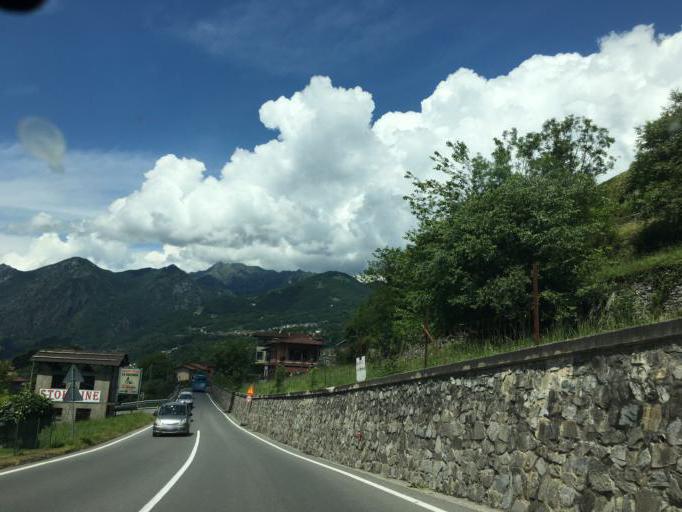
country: IT
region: Lombardy
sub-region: Provincia di Como
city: Bene Lario
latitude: 46.0392
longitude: 9.1772
